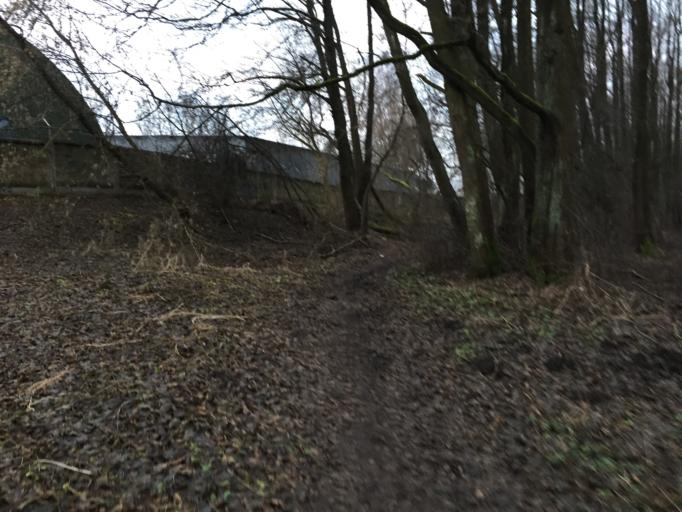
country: LV
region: Kekava
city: Kekava
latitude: 56.8970
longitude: 24.2004
